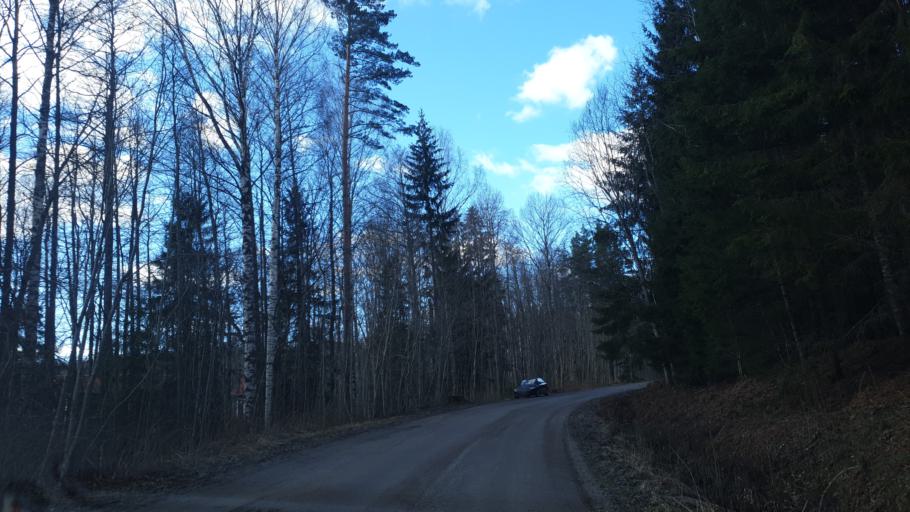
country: SE
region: OErebro
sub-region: Orebro Kommun
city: Garphyttan
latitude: 59.3500
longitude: 14.9894
